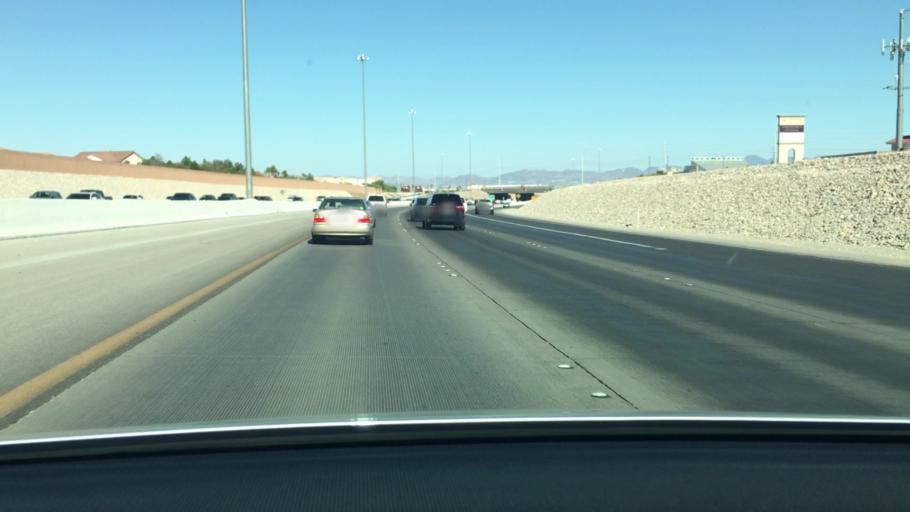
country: US
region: Nevada
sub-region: Clark County
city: Summerlin South
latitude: 36.1179
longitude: -115.3092
